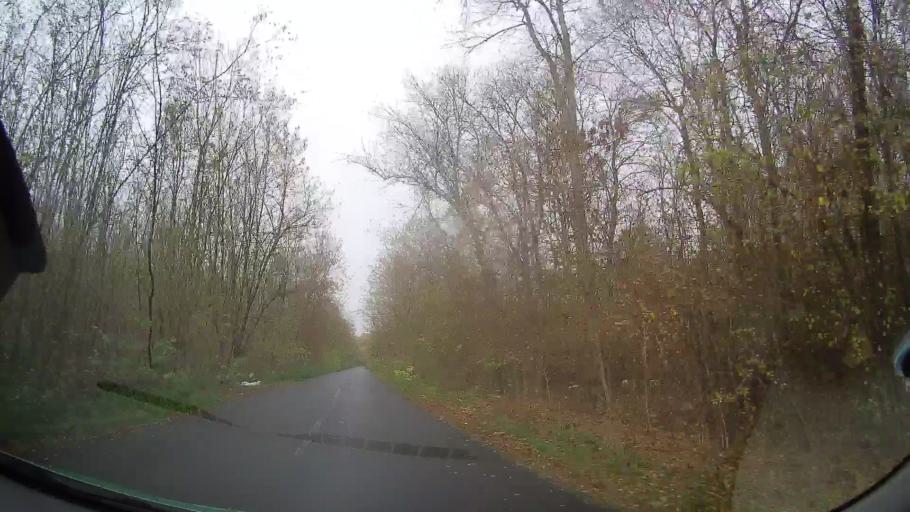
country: RO
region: Prahova
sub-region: Comuna Balta Doamnei
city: Balta Doamnei
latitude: 44.7579
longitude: 26.1303
